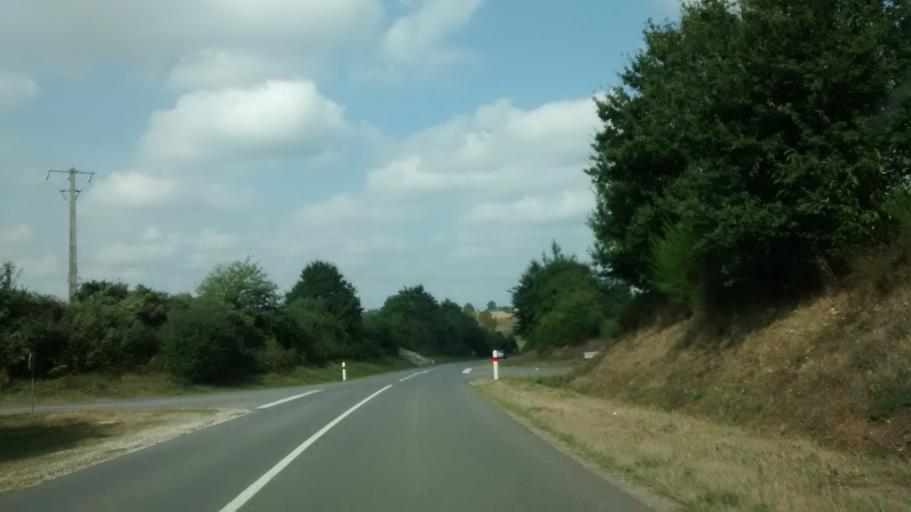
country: FR
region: Brittany
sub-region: Departement d'Ille-et-Vilaine
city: Livre-sur-Changeon
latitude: 48.2256
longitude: -1.3517
